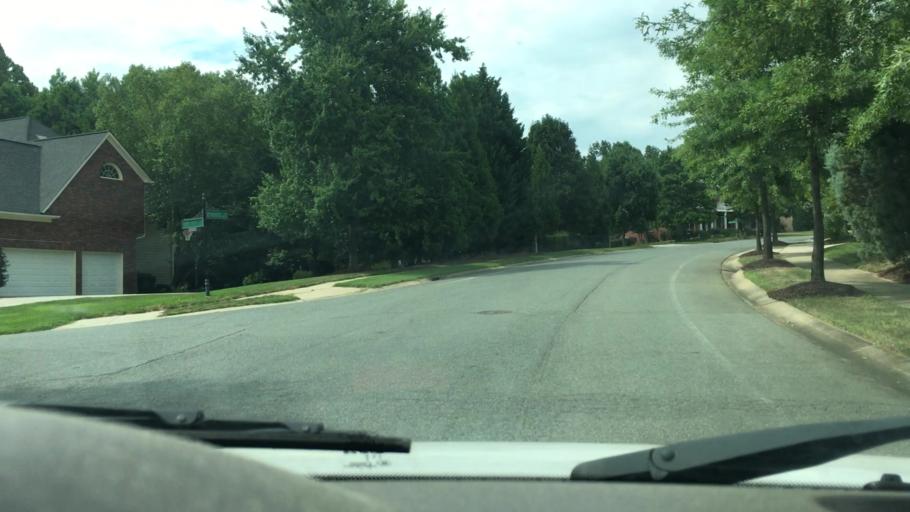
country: US
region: North Carolina
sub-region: Gaston County
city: Davidson
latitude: 35.4644
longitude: -80.7839
